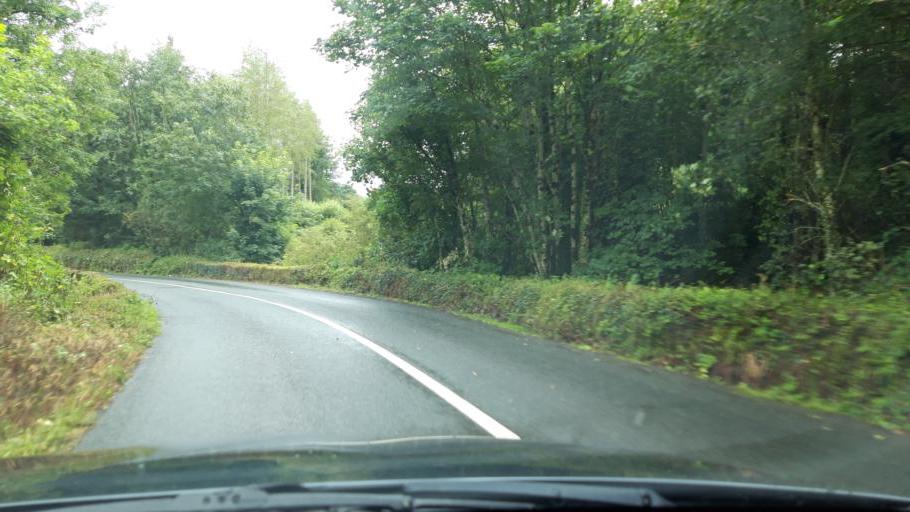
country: IE
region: Munster
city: Cahir
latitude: 52.1741
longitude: -7.8707
